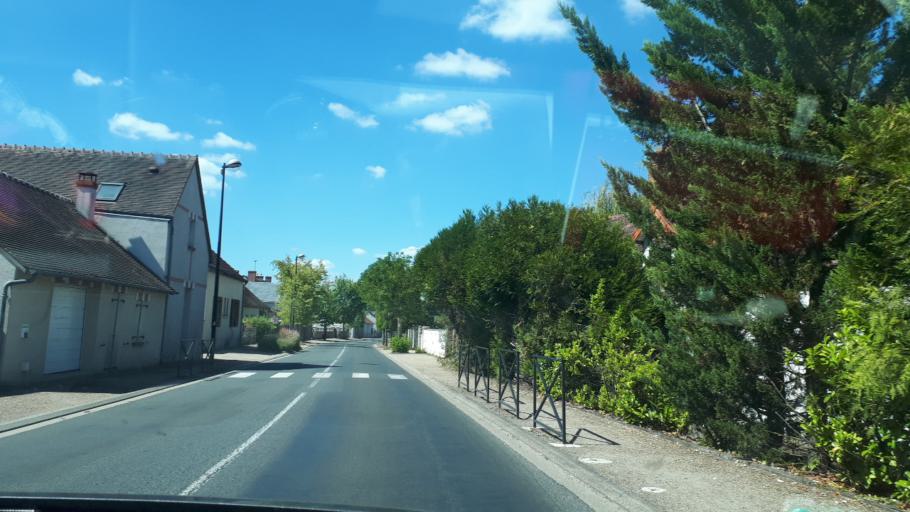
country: FR
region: Centre
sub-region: Departement du Loir-et-Cher
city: Mont-pres-Chambord
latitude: 47.5628
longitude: 1.4603
